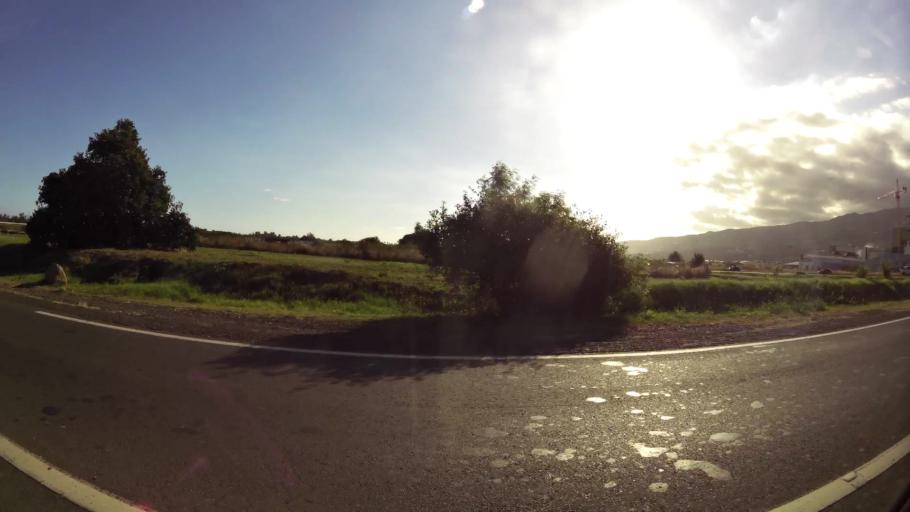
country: RE
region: Reunion
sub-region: Reunion
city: Saint-Louis
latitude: -21.2833
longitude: 55.3980
